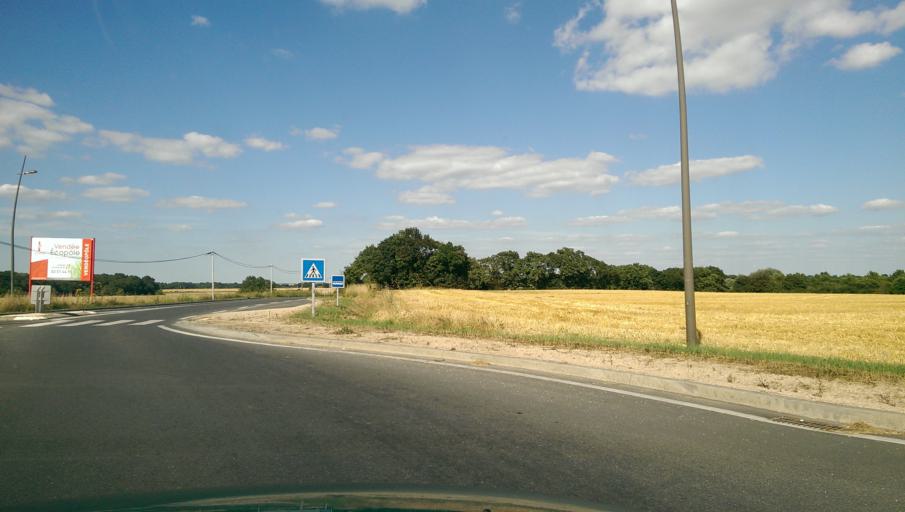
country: FR
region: Pays de la Loire
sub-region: Departement de la Vendee
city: Rocheserviere
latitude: 46.9463
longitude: -1.4906
